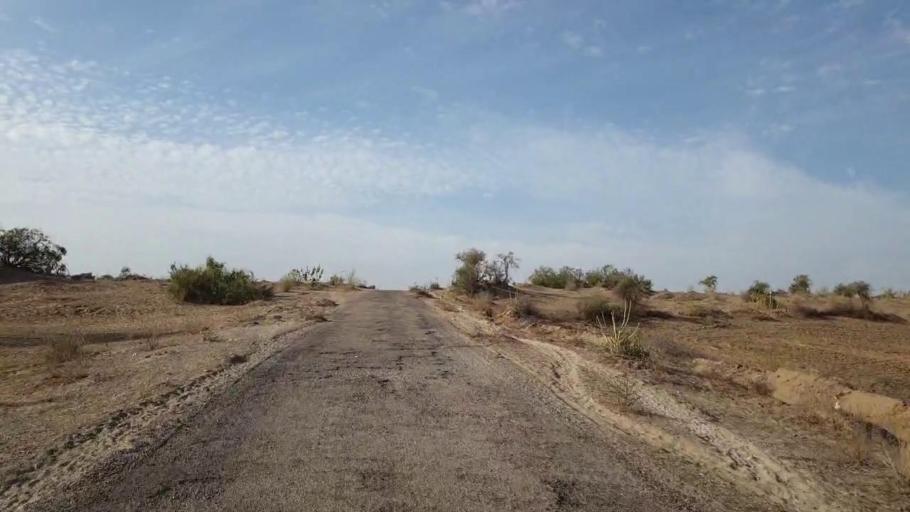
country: PK
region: Sindh
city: Nabisar
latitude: 25.0023
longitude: 69.9240
